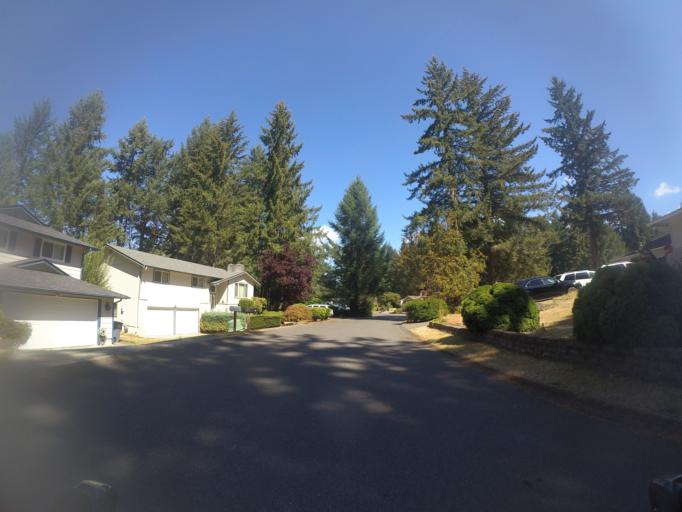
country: US
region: Washington
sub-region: Pierce County
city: University Place
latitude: 47.2151
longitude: -122.5574
